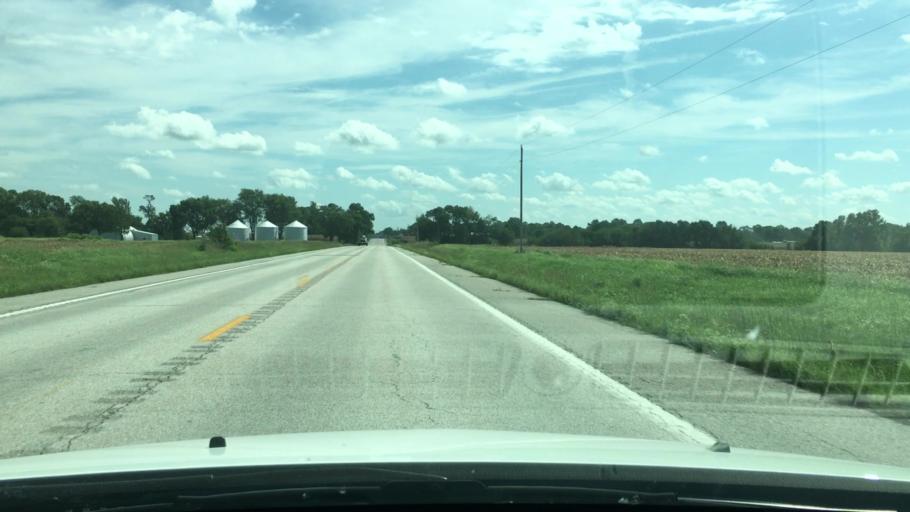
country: US
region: Missouri
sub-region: Audrain County
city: Vandalia
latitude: 39.2796
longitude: -91.5883
